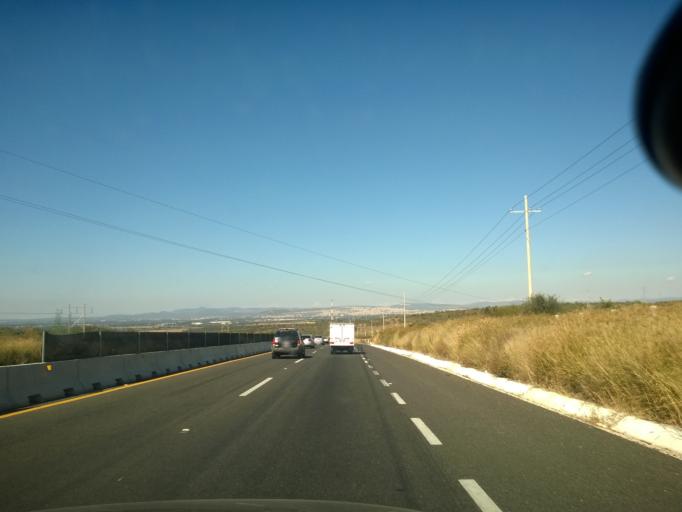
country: MX
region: Jalisco
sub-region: Lagos de Moreno
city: Geovillas Laureles del Campanario
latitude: 21.2981
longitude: -101.8673
